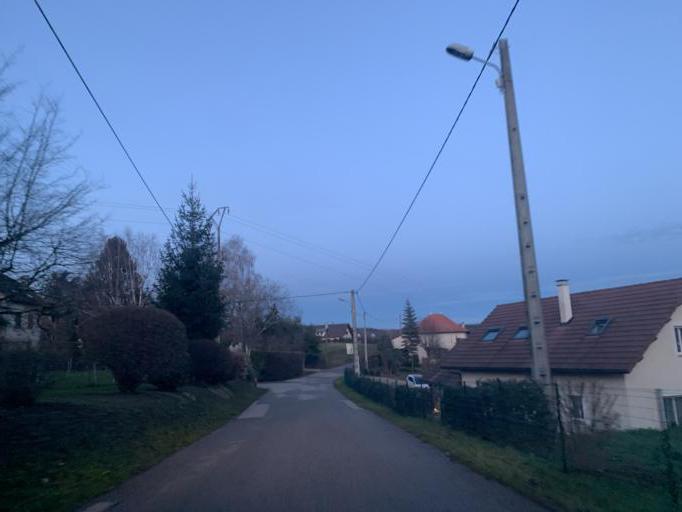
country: FR
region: Rhone-Alpes
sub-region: Departement de l'Ain
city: Belley
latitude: 45.7694
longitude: 5.6985
